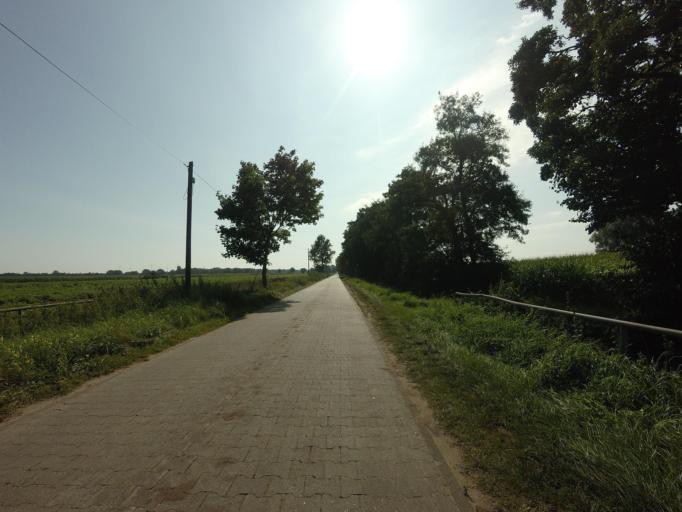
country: DE
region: Lower Saxony
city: Wilsum
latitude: 52.5694
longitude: 6.8224
